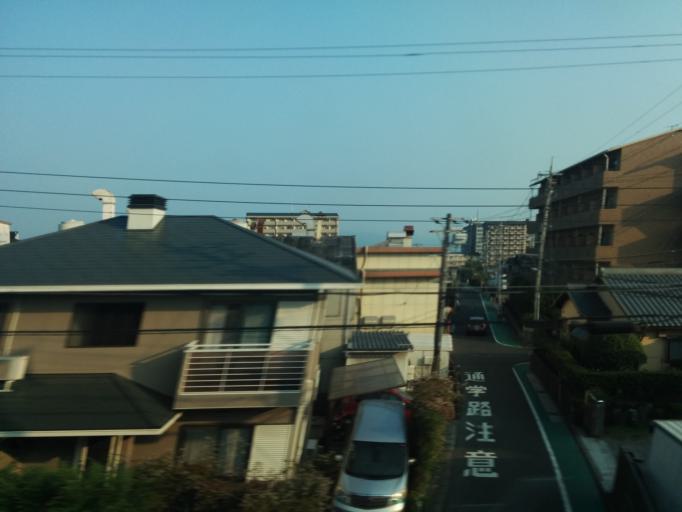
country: JP
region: Shiga Prefecture
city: Kusatsu
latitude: 34.9857
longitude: 135.9458
